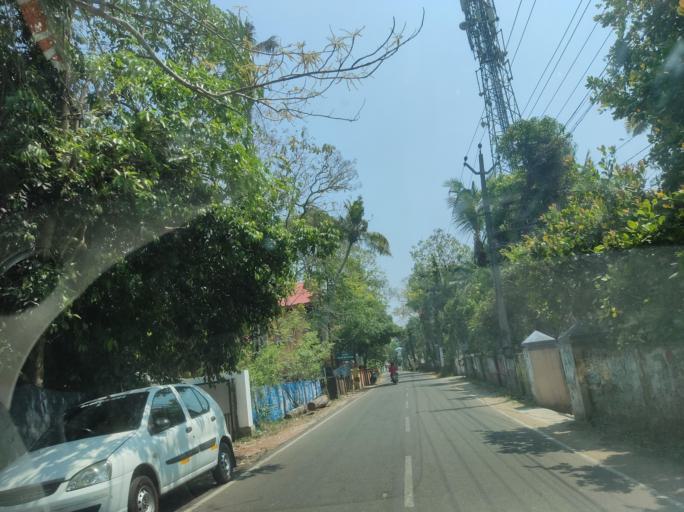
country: IN
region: Kerala
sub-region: Alappuzha
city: Kutiatodu
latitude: 9.7968
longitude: 76.3021
